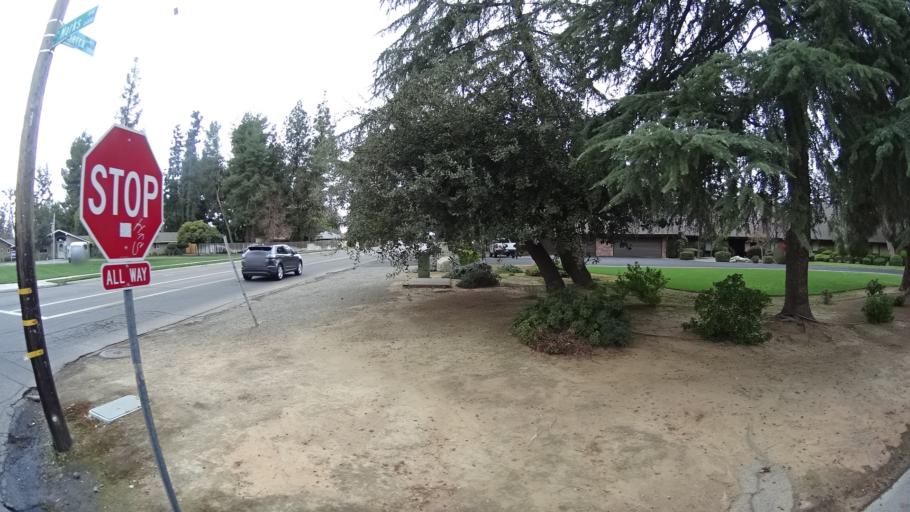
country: US
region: California
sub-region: Fresno County
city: Fresno
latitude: 36.8301
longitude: -119.8445
